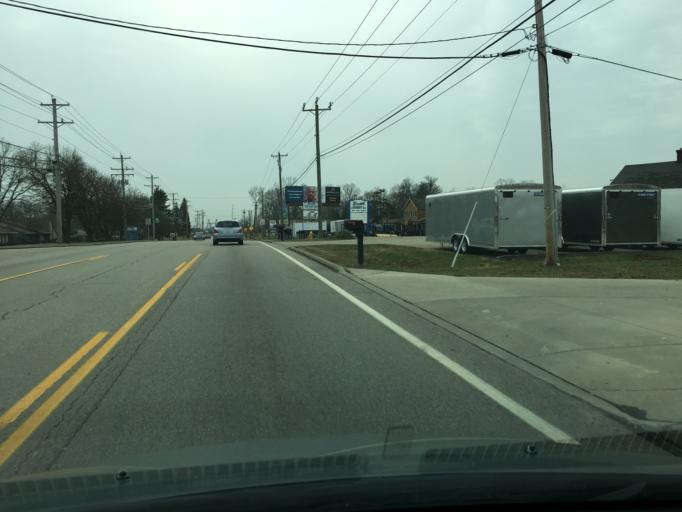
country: US
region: Ohio
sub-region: Hamilton County
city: Highpoint
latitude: 39.3101
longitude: -84.3812
